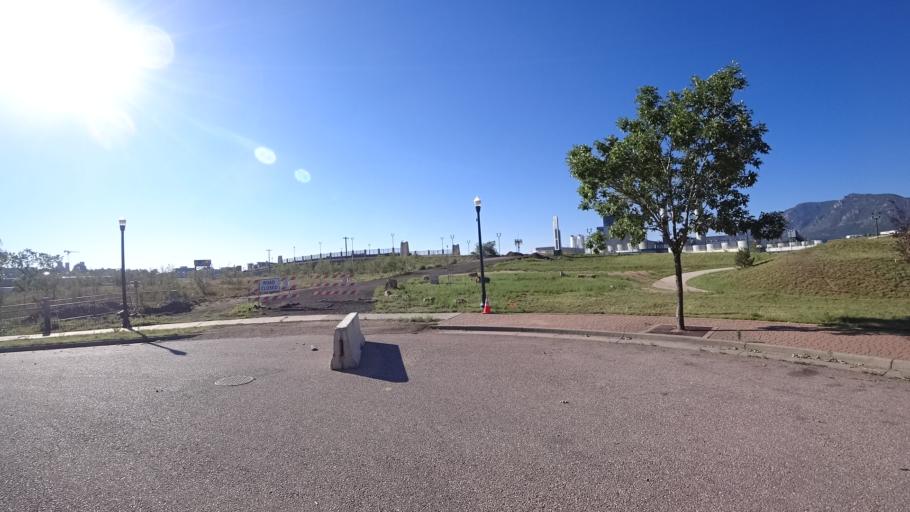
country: US
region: Colorado
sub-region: El Paso County
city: Colorado Springs
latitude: 38.8281
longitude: -104.8327
